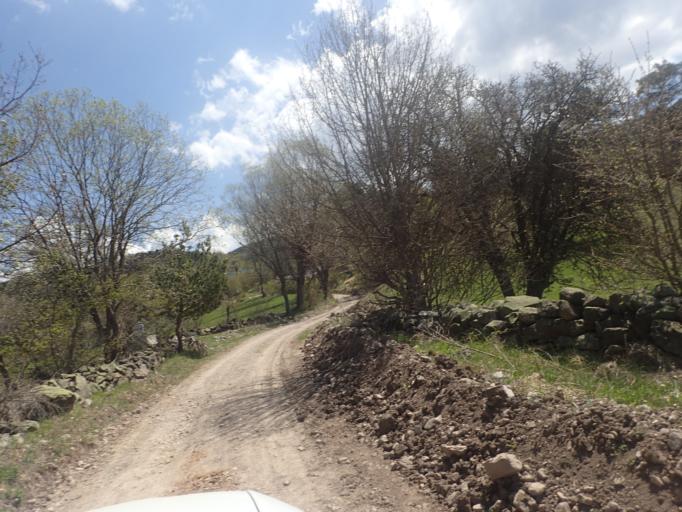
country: TR
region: Ordu
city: Mesudiye
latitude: 40.4169
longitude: 37.8431
